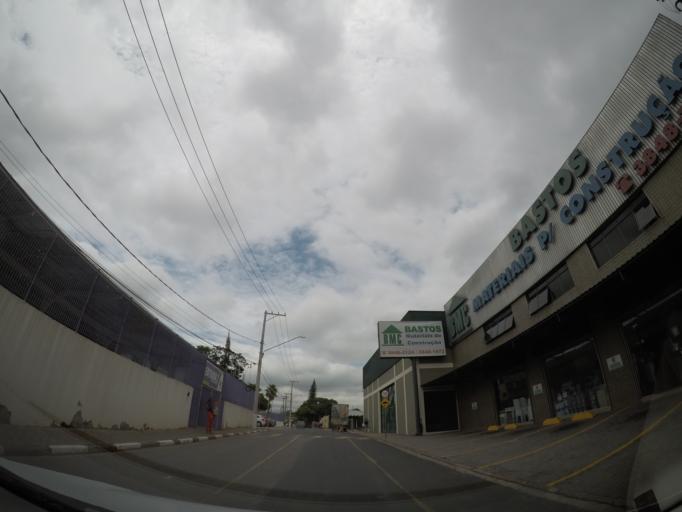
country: BR
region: Sao Paulo
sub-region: Louveira
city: Louveira
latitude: -23.0876
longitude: -46.9813
